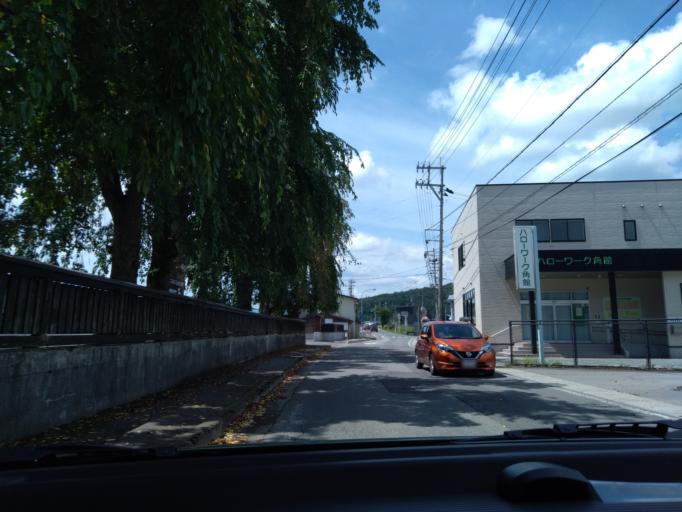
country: JP
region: Akita
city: Kakunodatemachi
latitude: 39.5907
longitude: 140.5617
